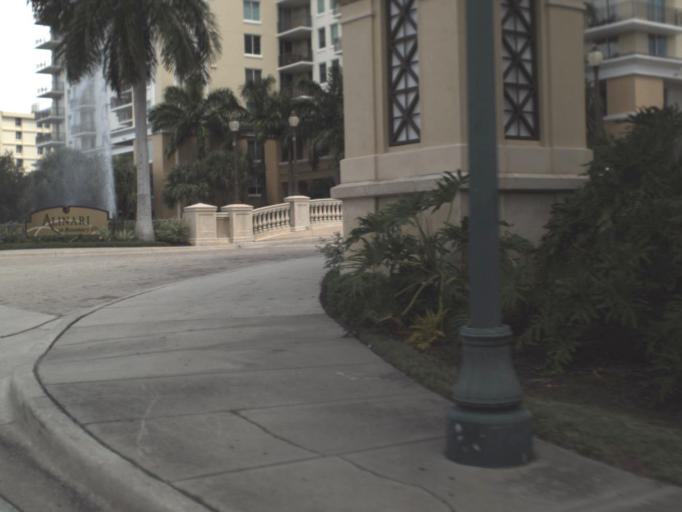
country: US
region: Florida
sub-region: Sarasota County
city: Sarasota
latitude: 27.3425
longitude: -82.5467
